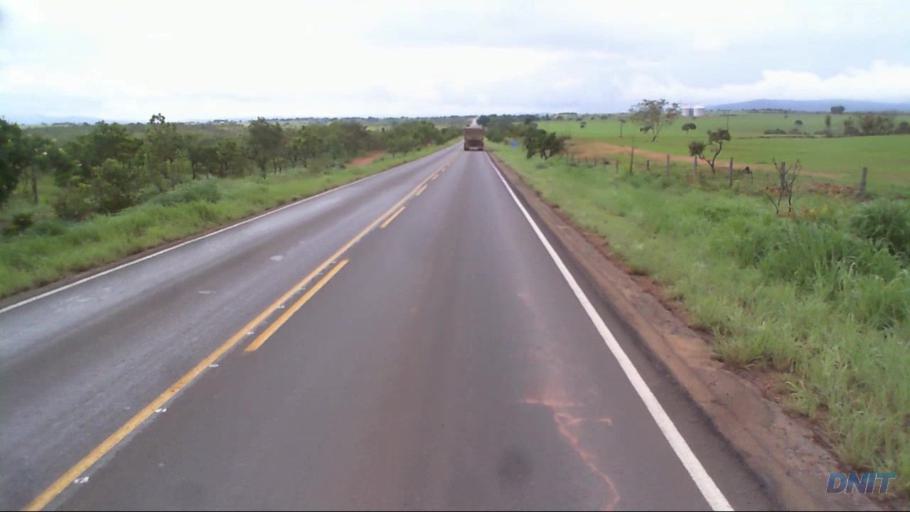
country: BR
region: Goias
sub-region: Padre Bernardo
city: Padre Bernardo
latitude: -15.2282
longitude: -48.2773
